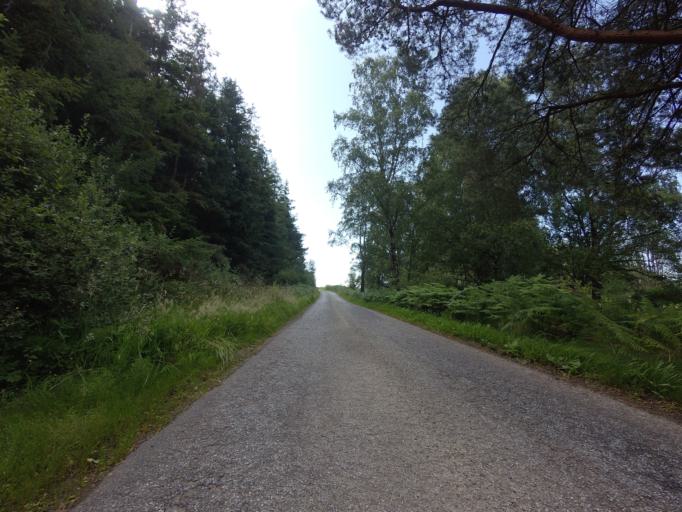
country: GB
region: Scotland
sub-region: Highland
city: Nairn
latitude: 57.5353
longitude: -3.8660
